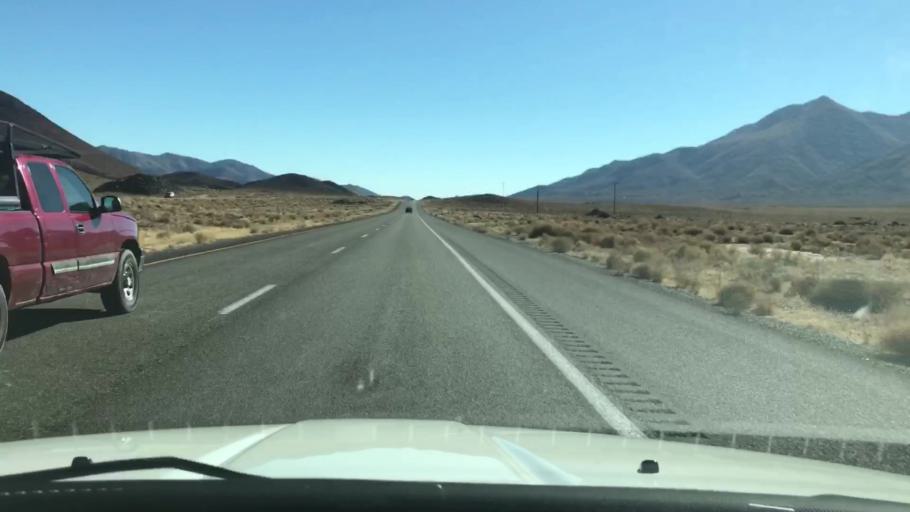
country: US
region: California
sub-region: Kern County
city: Inyokern
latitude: 35.9982
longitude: -117.9328
